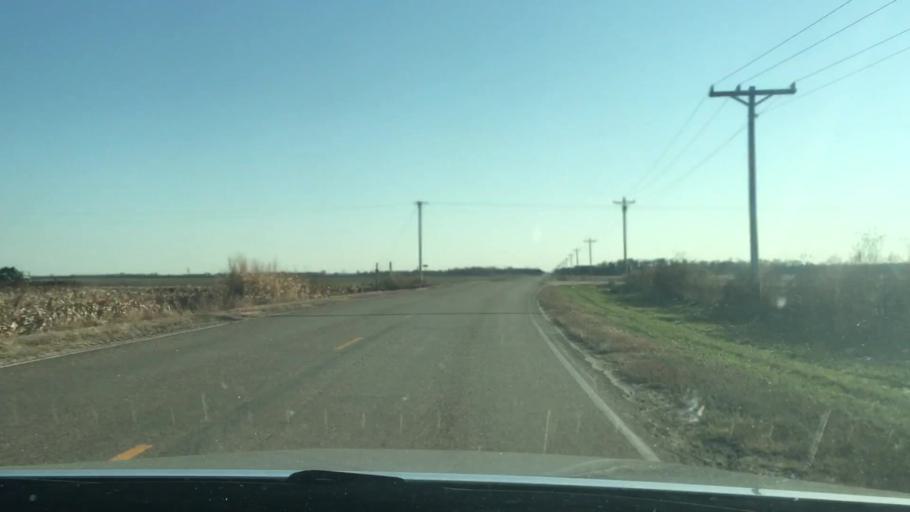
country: US
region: Kansas
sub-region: Reno County
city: Nickerson
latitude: 38.2612
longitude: -98.0878
